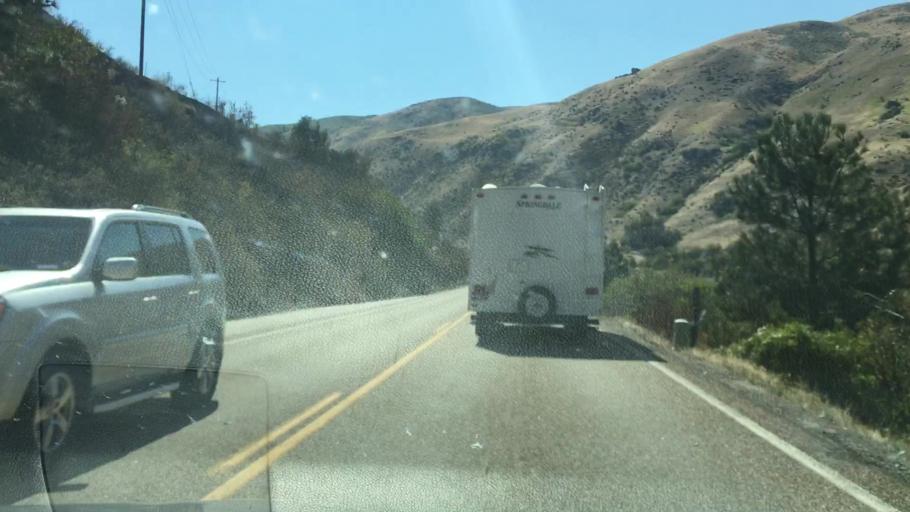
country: US
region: Idaho
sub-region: Gem County
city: Emmett
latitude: 44.0074
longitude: -116.1741
